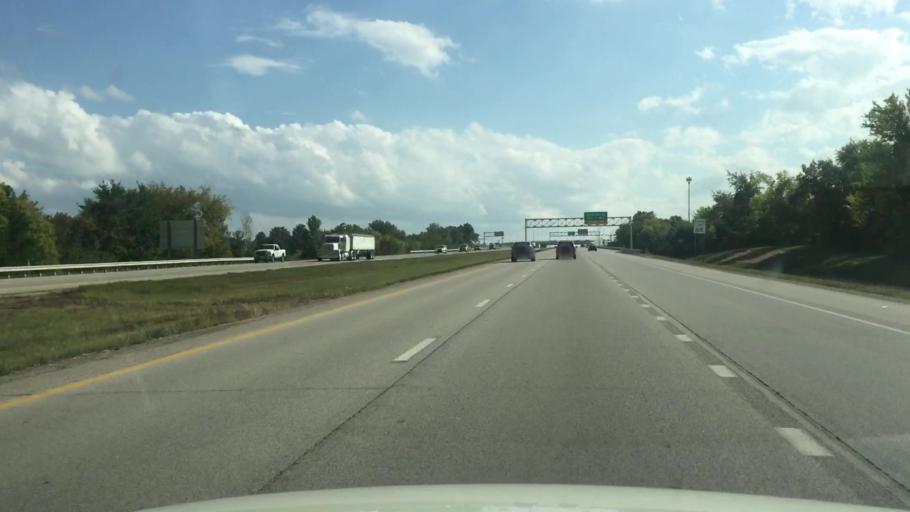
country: US
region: Kansas
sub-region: Johnson County
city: Lenexa
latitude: 38.8479
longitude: -94.6770
